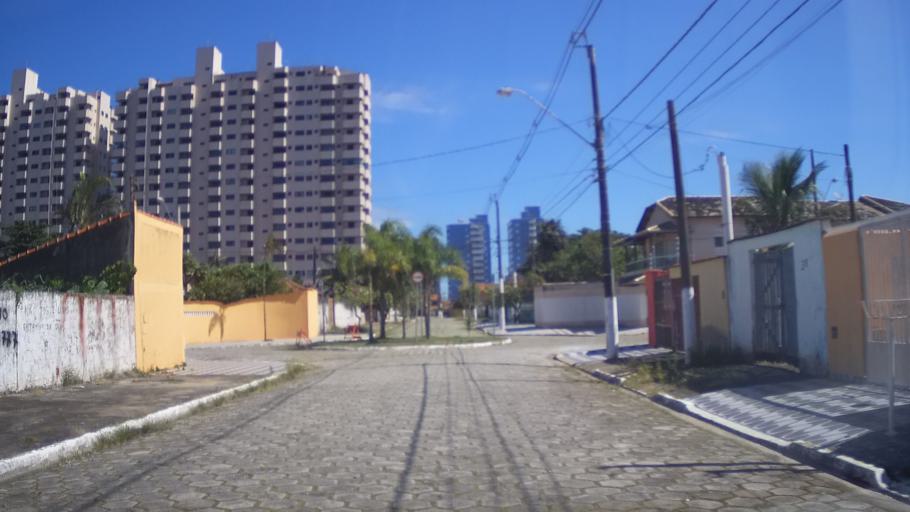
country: BR
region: Sao Paulo
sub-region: Praia Grande
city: Praia Grande
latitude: -24.0400
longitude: -46.5046
